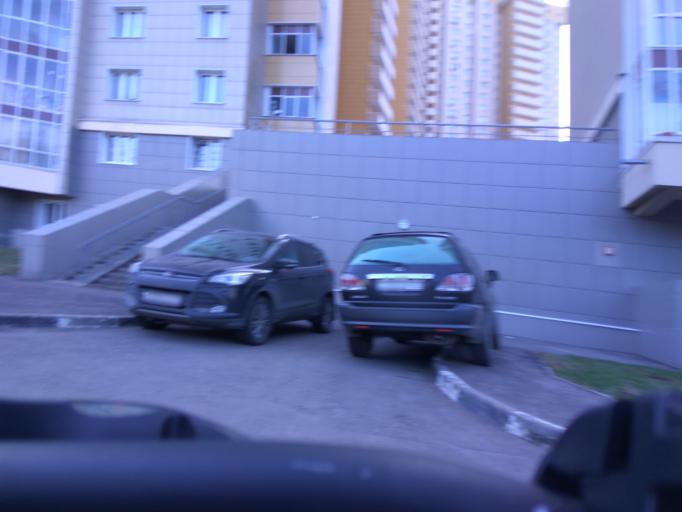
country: RU
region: Moscow
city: Davydkovo
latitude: 55.7250
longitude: 37.4685
